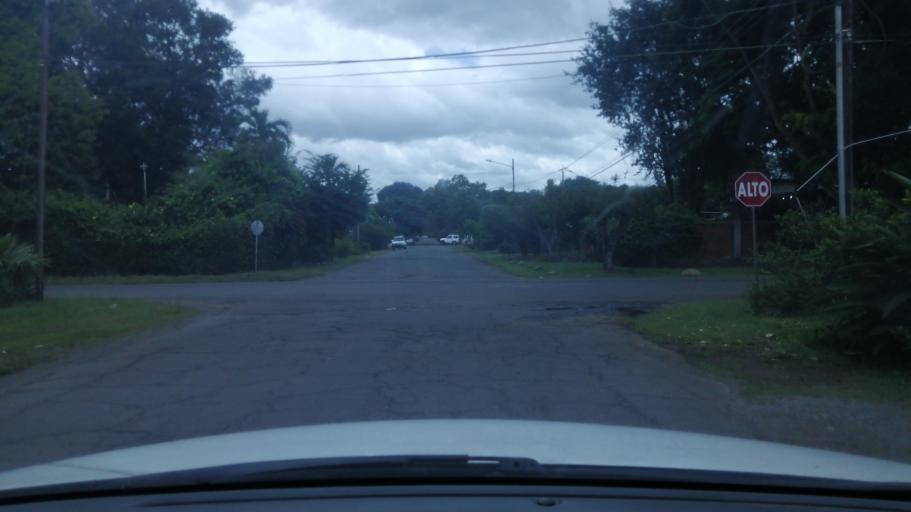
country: PA
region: Chiriqui
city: David
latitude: 8.4429
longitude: -82.4267
